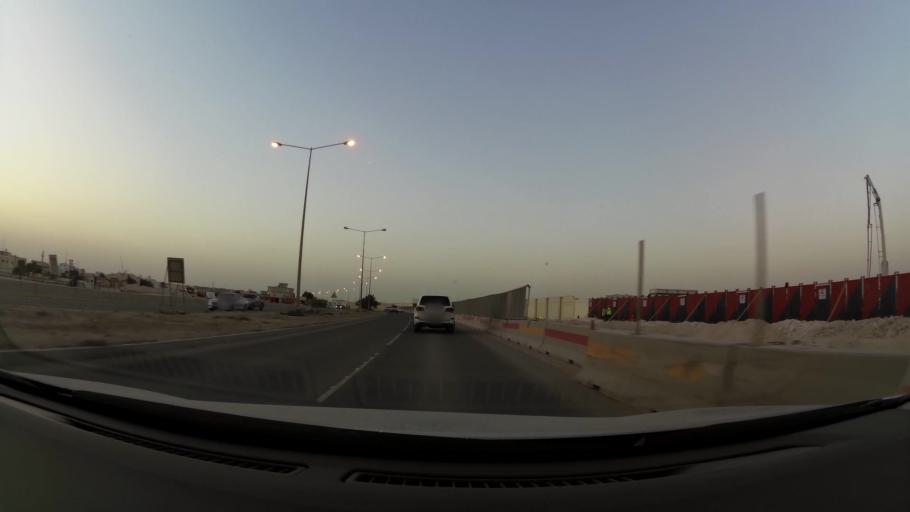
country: QA
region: Baladiyat ar Rayyan
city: Ar Rayyan
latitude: 25.3051
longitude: 51.4648
